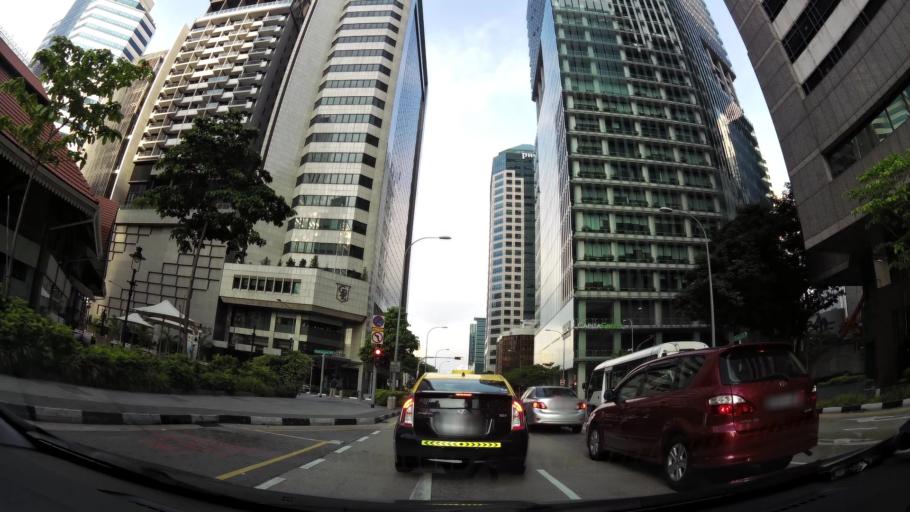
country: SG
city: Singapore
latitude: 1.2809
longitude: 103.8506
